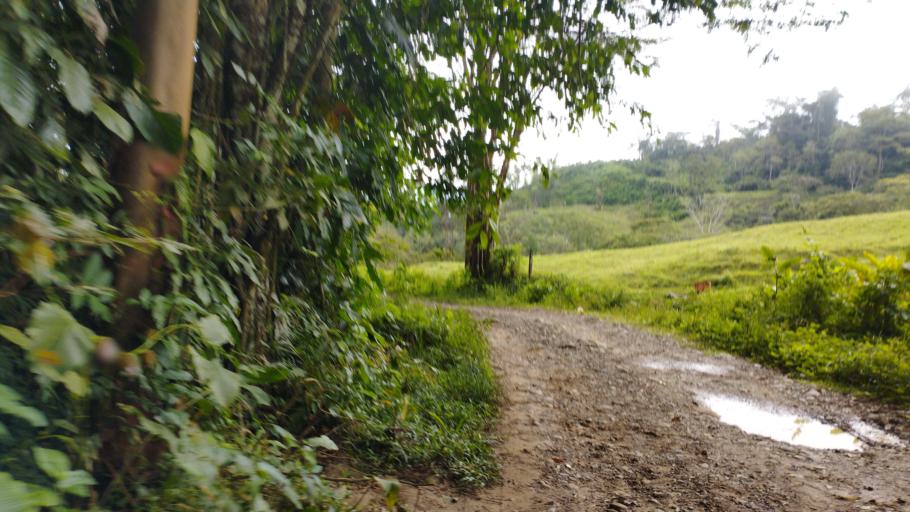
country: CO
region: Casanare
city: Sabanalarga
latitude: 4.7563
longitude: -73.0804
